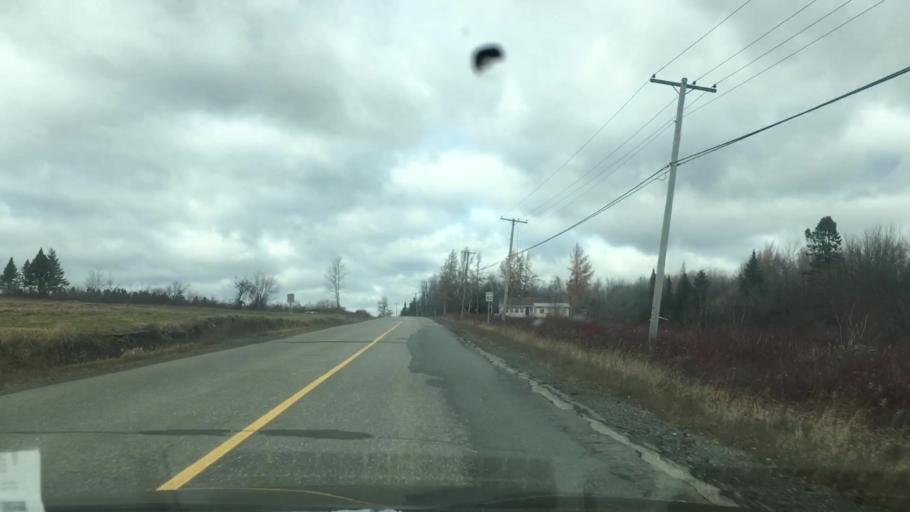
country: US
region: Maine
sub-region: Aroostook County
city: Fort Fairfield
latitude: 46.7526
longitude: -67.7578
